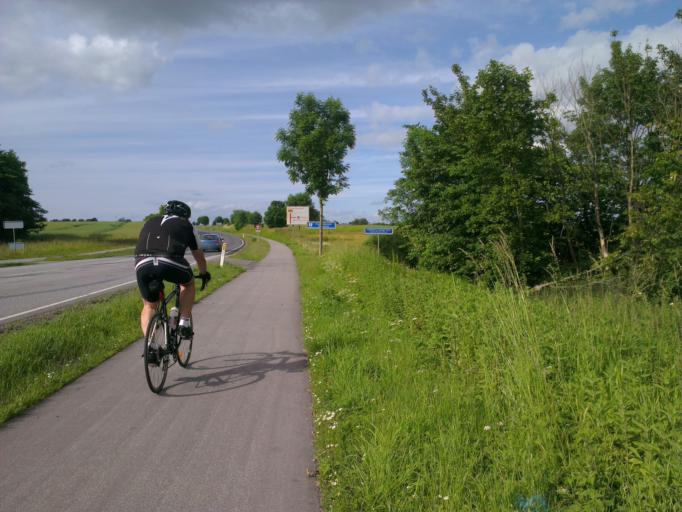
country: DK
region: Capital Region
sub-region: Frederikssund Kommune
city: Skibby
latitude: 55.7378
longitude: 11.9501
